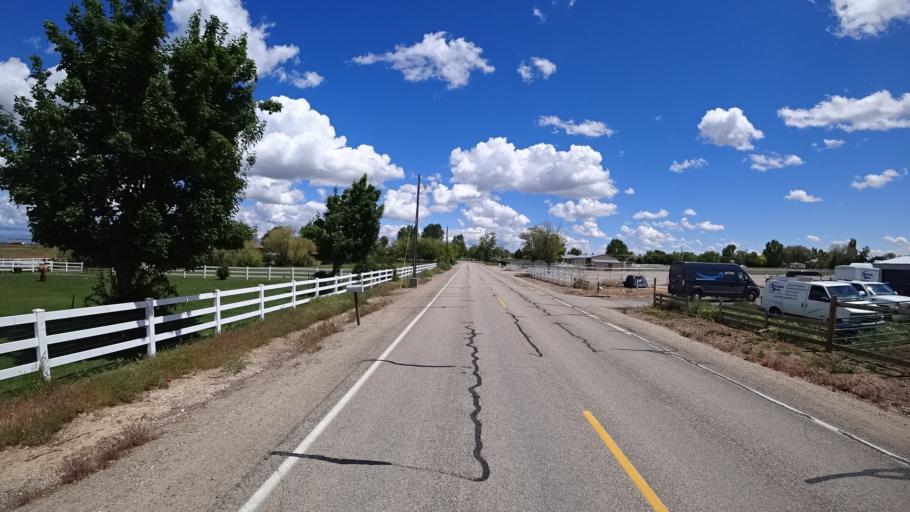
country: US
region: Idaho
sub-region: Ada County
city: Meridian
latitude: 43.5830
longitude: -116.4358
